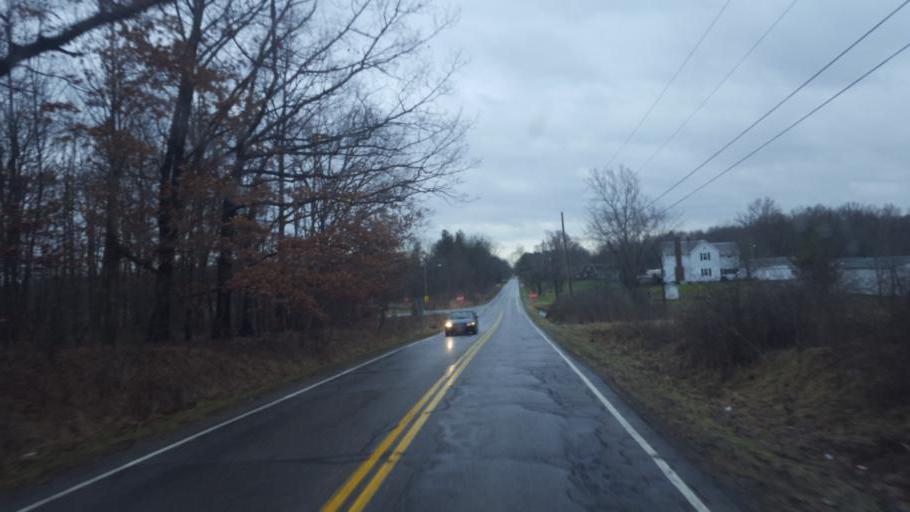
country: US
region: Ohio
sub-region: Portage County
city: Garrettsville
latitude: 41.3560
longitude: -80.9747
